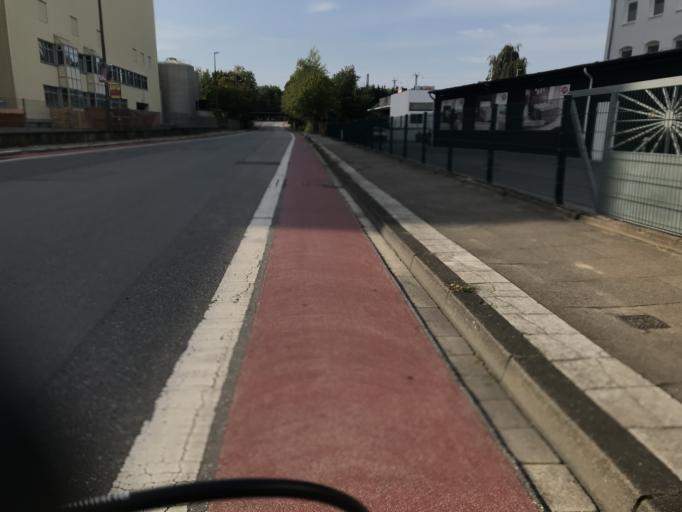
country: DE
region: North Rhine-Westphalia
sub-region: Regierungsbezirk Detmold
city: Herford
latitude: 52.1096
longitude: 8.6566
